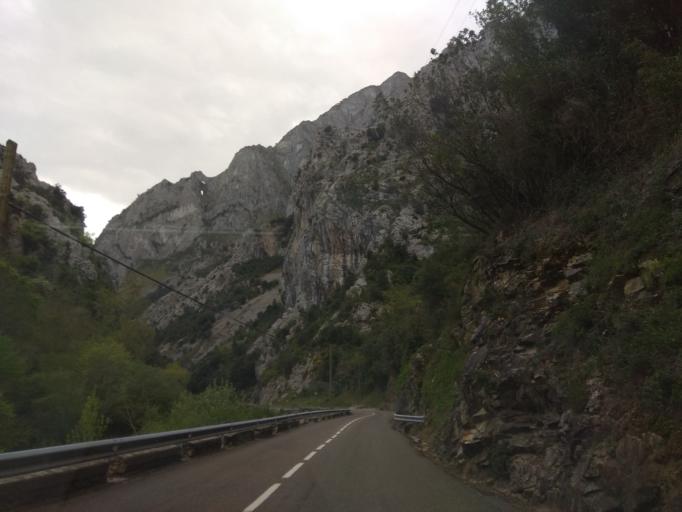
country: ES
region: Cantabria
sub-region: Provincia de Cantabria
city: Tresviso
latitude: 43.2761
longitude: -4.6362
